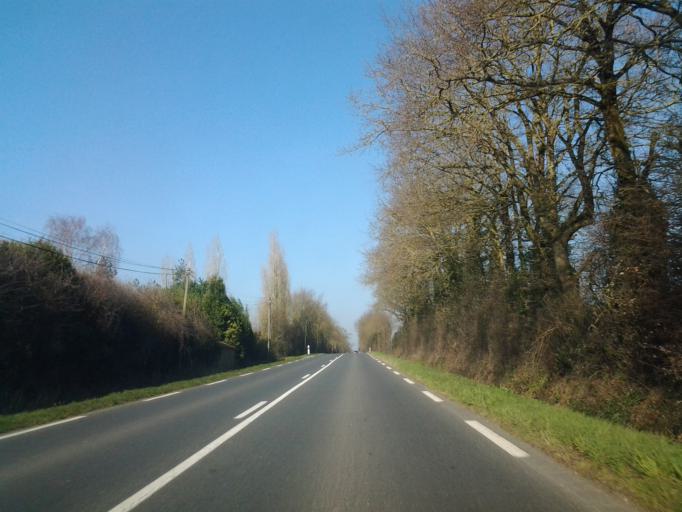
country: FR
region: Pays de la Loire
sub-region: Departement de la Vendee
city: Mache
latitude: 46.7828
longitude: -1.6912
